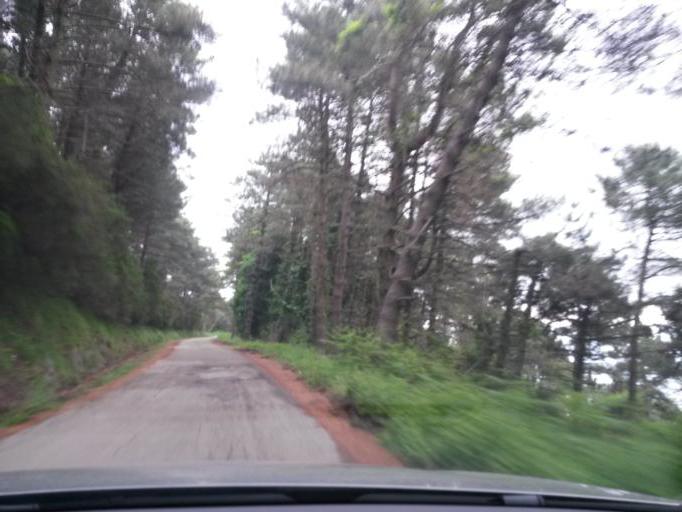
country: IT
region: Tuscany
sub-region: Provincia di Livorno
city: Marciana Marina
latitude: 42.7756
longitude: 10.1974
